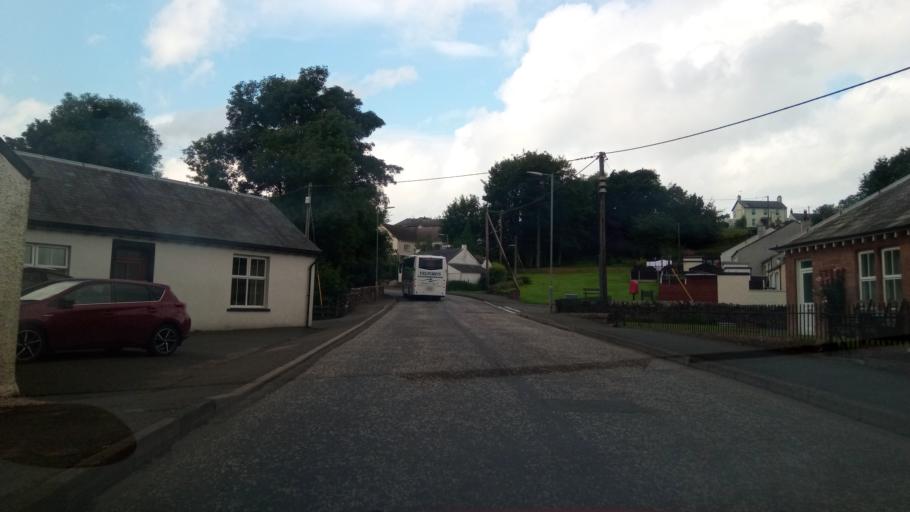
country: GB
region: Scotland
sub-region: Dumfries and Galloway
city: Langholm
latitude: 55.0788
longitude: -2.9523
